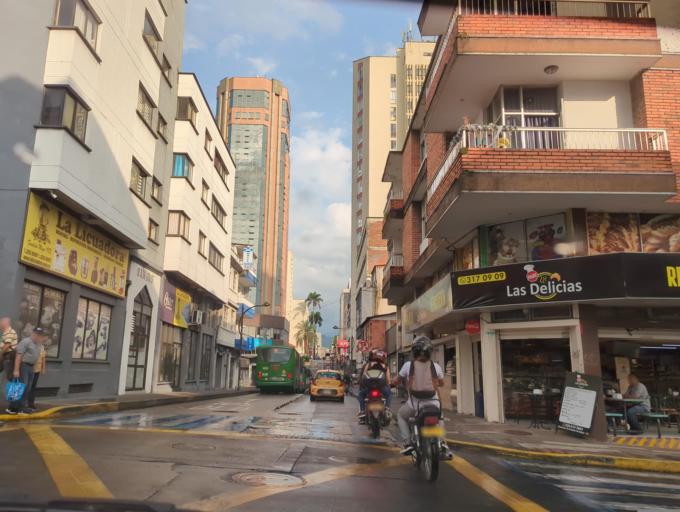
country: CO
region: Risaralda
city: Pereira
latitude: 4.8124
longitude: -75.6962
